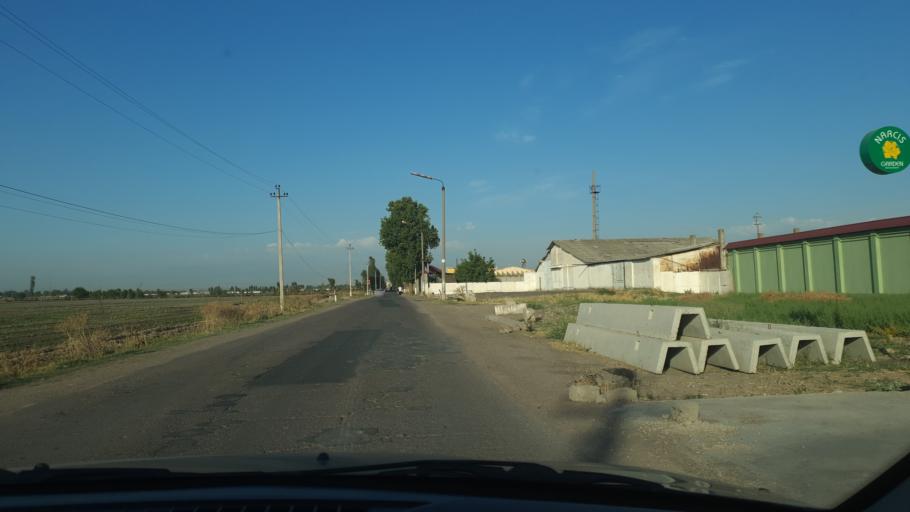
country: UZ
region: Toshkent
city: Tuytepa
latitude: 41.0848
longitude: 69.3366
